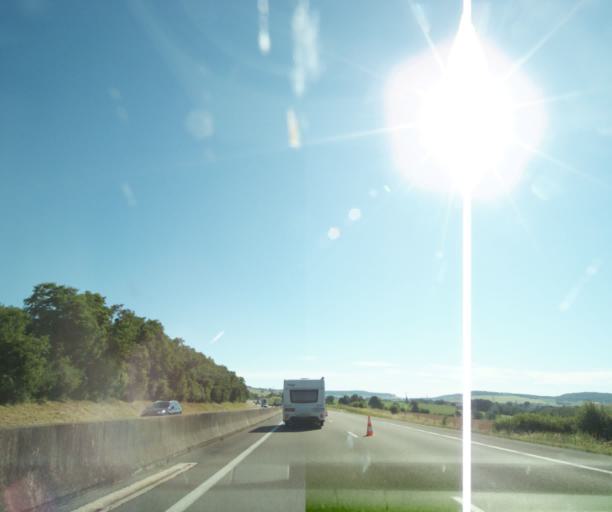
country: FR
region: Champagne-Ardenne
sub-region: Departement de la Haute-Marne
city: Rolampont
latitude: 47.9487
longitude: 5.3445
